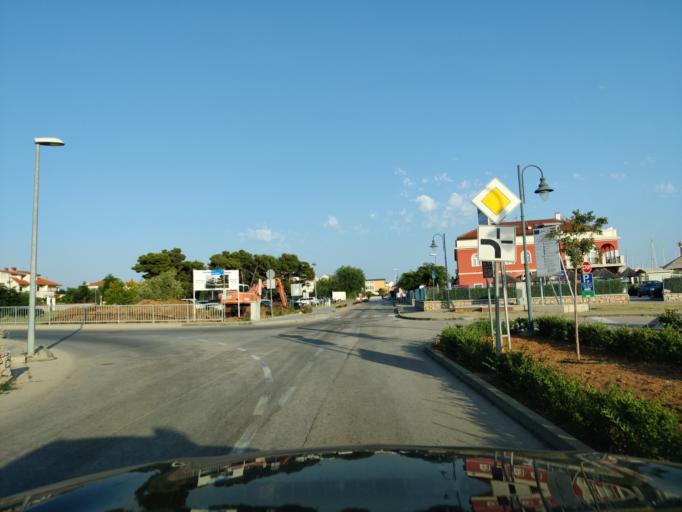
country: HR
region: Sibensko-Kniniska
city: Tribunj
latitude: 43.7561
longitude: 15.7460
